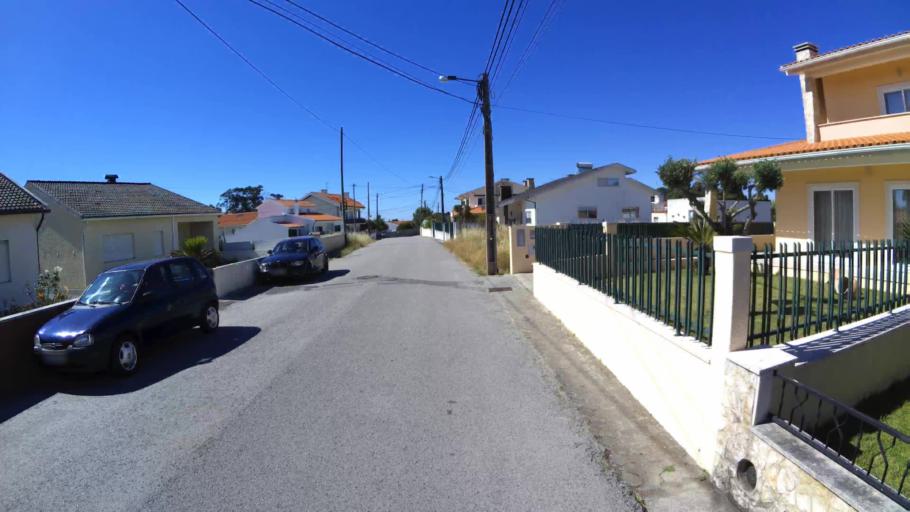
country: PT
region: Aveiro
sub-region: Aveiro
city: Aveiro
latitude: 40.6626
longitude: -8.6228
